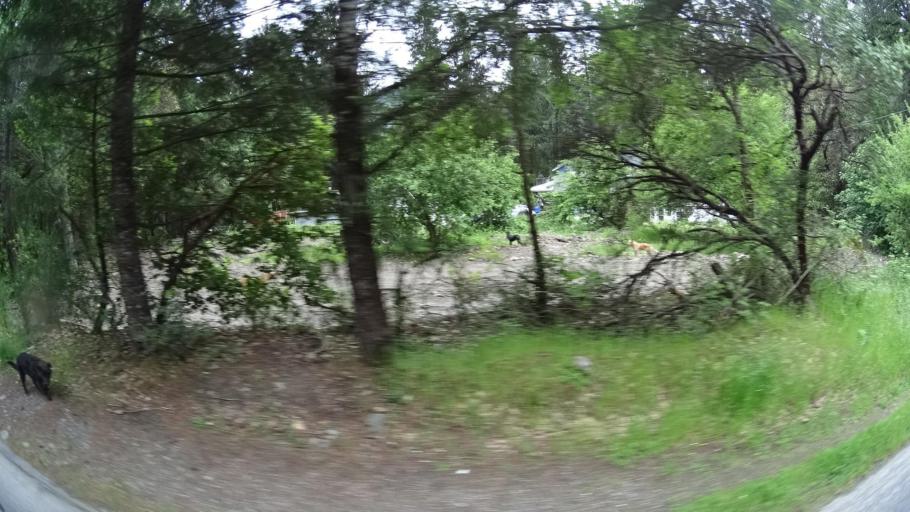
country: US
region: California
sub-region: Humboldt County
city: Willow Creek
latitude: 41.0523
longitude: -123.6698
